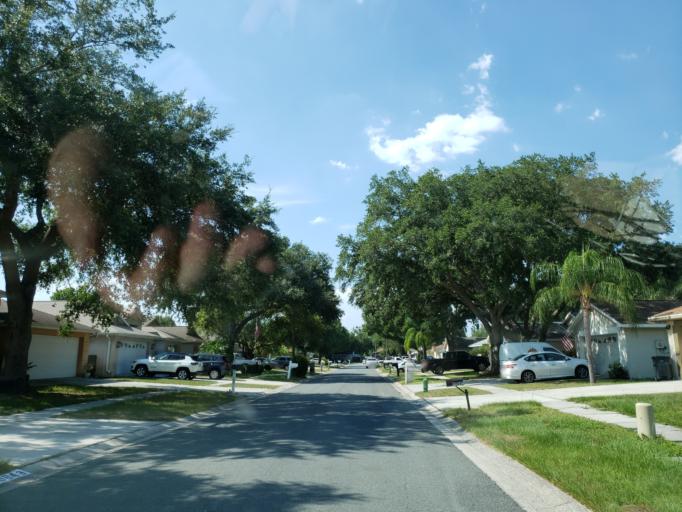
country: US
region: Florida
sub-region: Hillsborough County
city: Riverview
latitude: 27.8905
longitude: -82.3237
